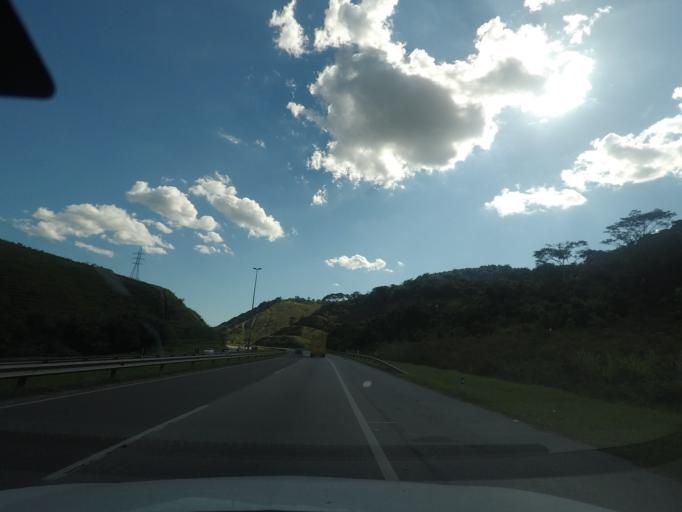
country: BR
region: Rio de Janeiro
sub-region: Guapimirim
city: Guapimirim
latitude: -22.5725
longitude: -43.0079
